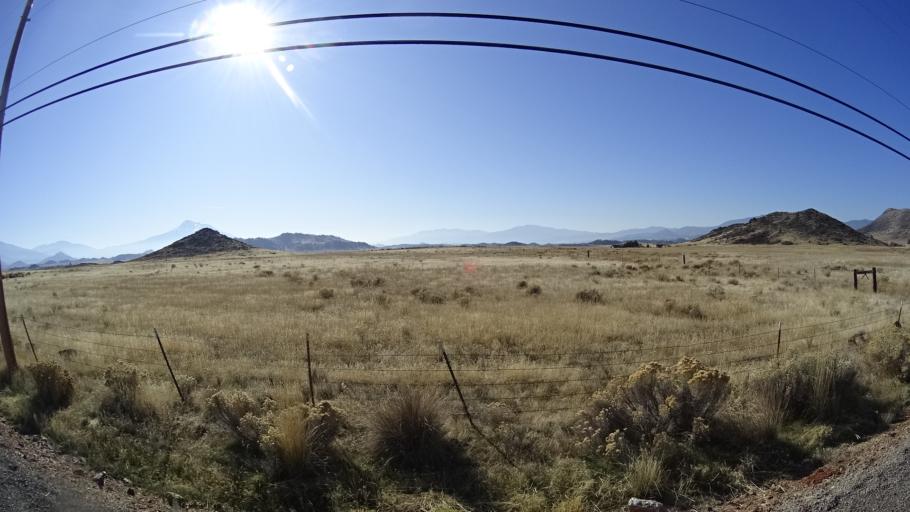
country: US
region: California
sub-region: Siskiyou County
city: Montague
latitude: 41.7269
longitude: -122.4849
